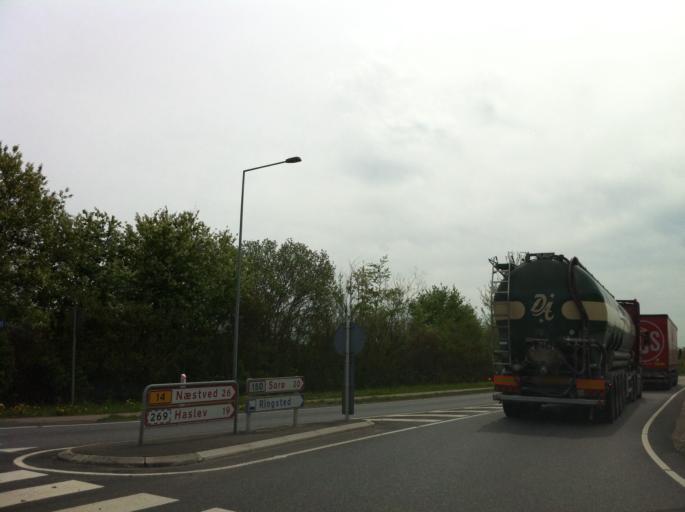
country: DK
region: Zealand
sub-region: Ringsted Kommune
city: Ringsted
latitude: 55.4448
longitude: 11.8252
